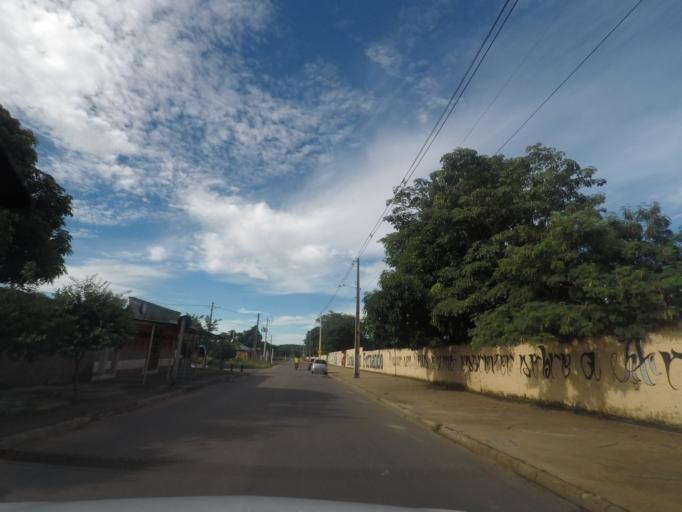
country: BR
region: Goias
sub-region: Aparecida De Goiania
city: Aparecida de Goiania
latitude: -16.8242
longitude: -49.2965
